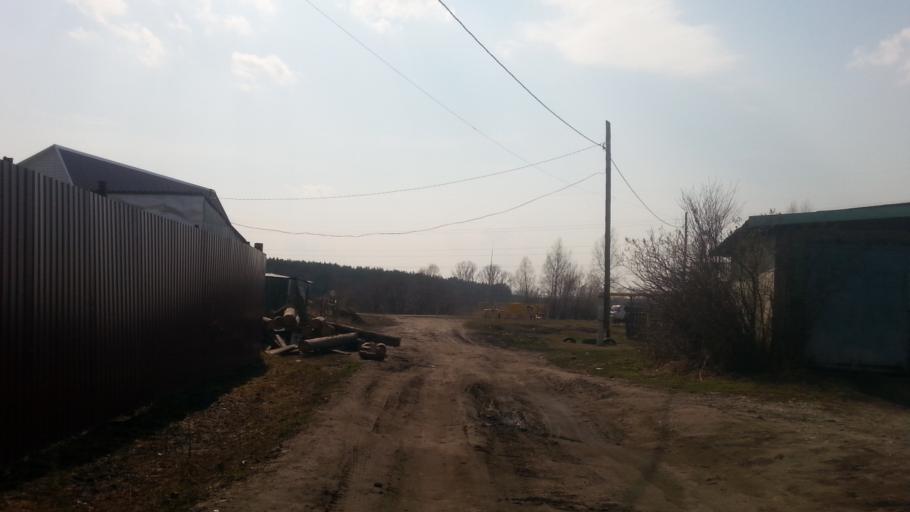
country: RU
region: Altai Krai
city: Yuzhnyy
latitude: 53.3090
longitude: 83.7158
